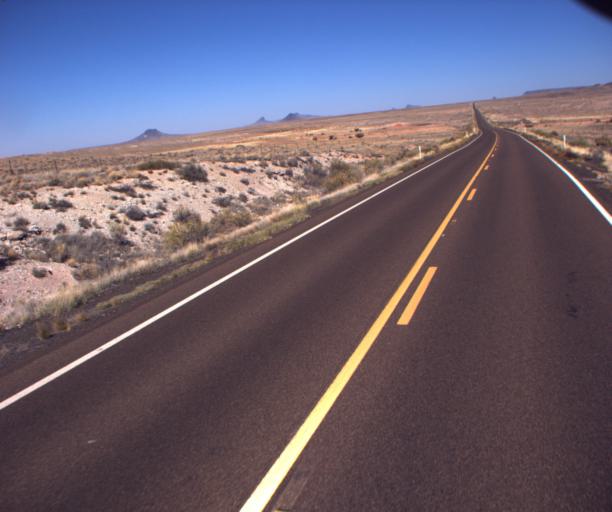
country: US
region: Arizona
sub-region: Navajo County
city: Dilkon
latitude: 35.2396
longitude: -110.4304
